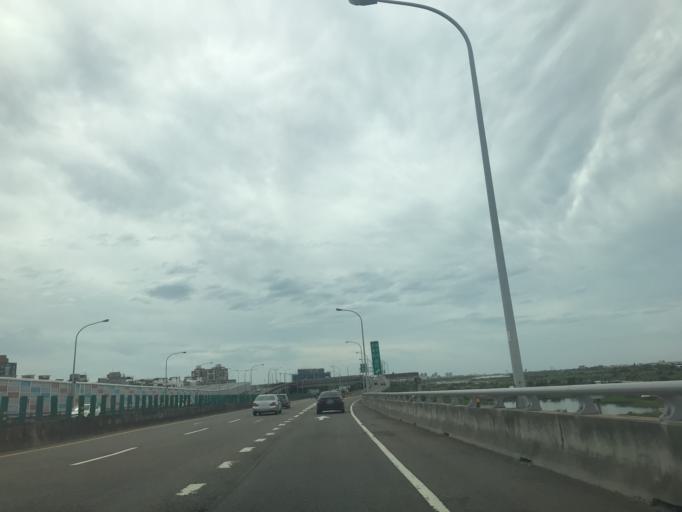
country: TW
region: Taiwan
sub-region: Hsinchu
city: Hsinchu
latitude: 24.8253
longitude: 120.9755
